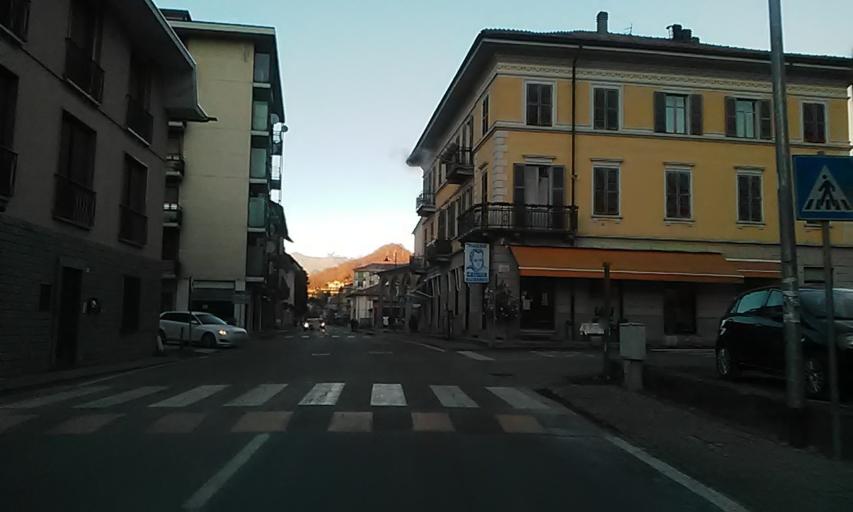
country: IT
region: Piedmont
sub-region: Provincia di Vercelli
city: Quarona
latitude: 45.7596
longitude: 8.2684
